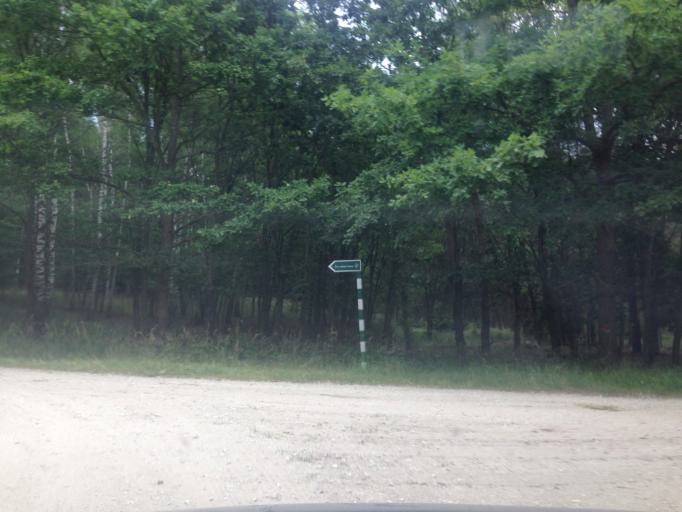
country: PL
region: Kujawsko-Pomorskie
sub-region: Powiat rypinski
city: Wapielsk
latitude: 53.1818
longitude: 19.1949
